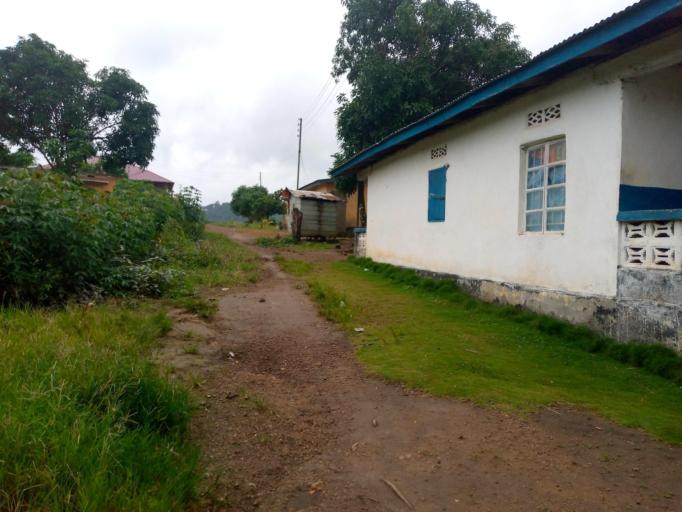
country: SL
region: Eastern Province
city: Kenema
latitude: 7.8437
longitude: -11.2016
